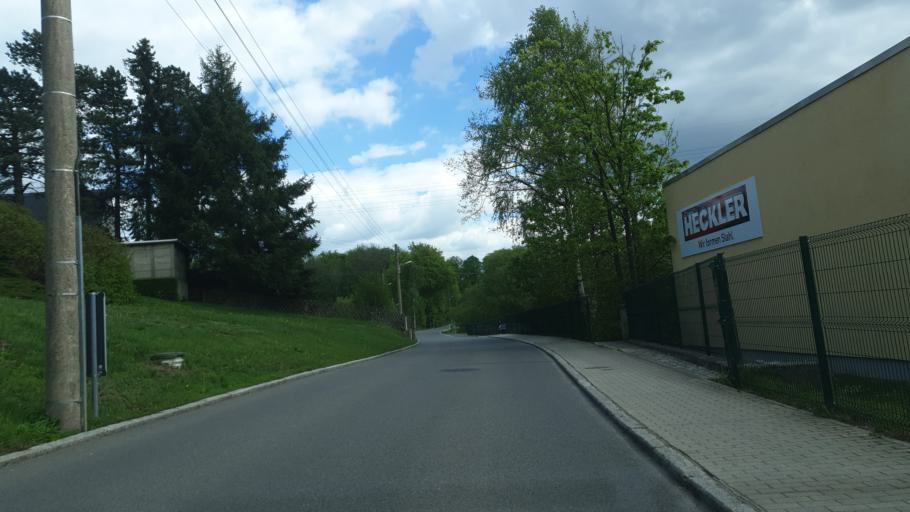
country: DE
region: Saxony
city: Kirchberg
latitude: 50.7879
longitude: 12.7673
